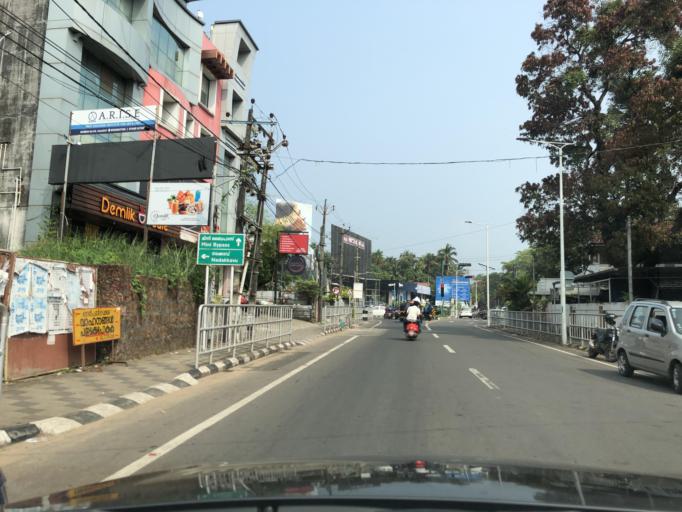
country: IN
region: Kerala
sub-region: Kozhikode
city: Kozhikode
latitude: 11.2643
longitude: 75.7765
